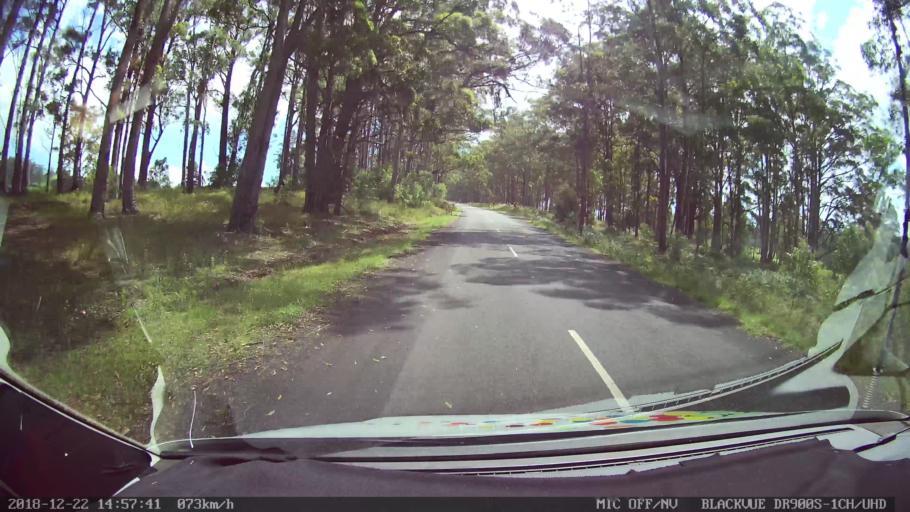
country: AU
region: New South Wales
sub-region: Bellingen
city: Dorrigo
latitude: -30.2357
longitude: 152.4984
